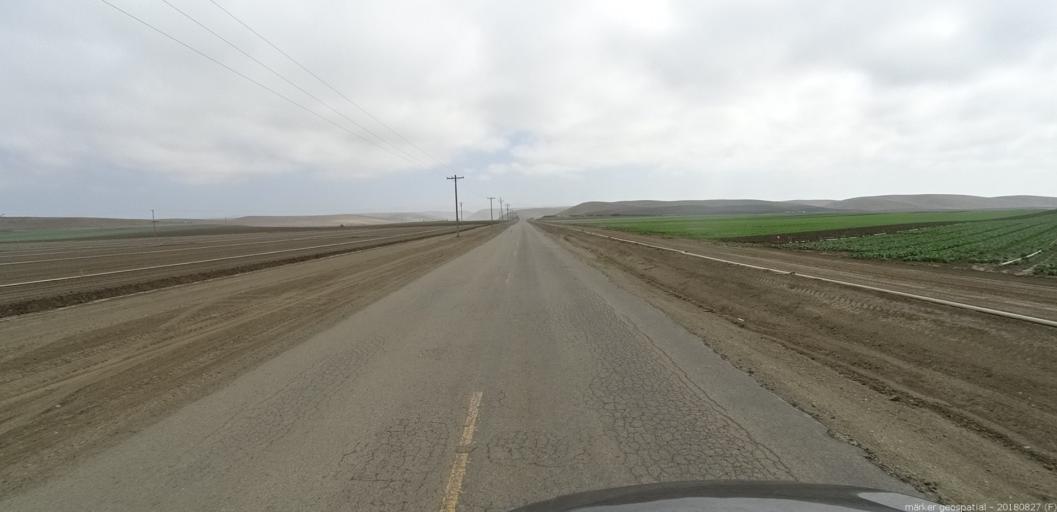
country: US
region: California
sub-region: Monterey County
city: King City
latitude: 36.2171
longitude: -121.0882
